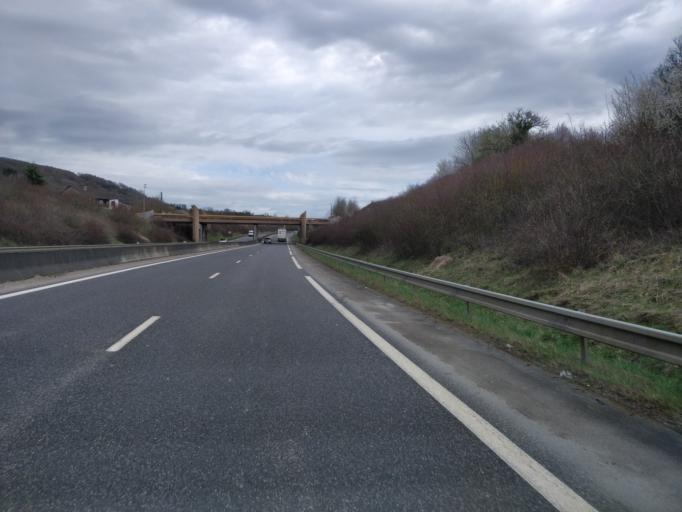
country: FR
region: Lorraine
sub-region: Departement de la Moselle
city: Vitry-sur-Orne
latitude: 49.2696
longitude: 6.1104
